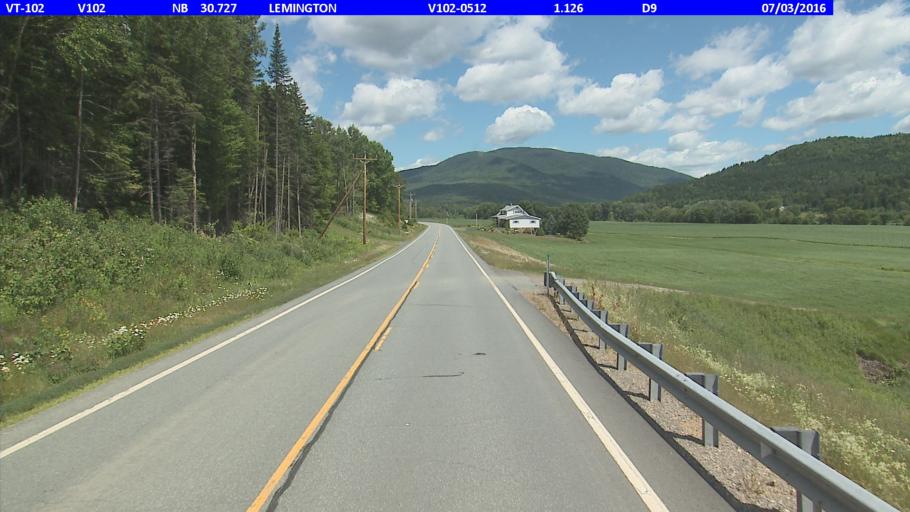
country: US
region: New Hampshire
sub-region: Coos County
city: Colebrook
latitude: 44.8406
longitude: -71.5565
